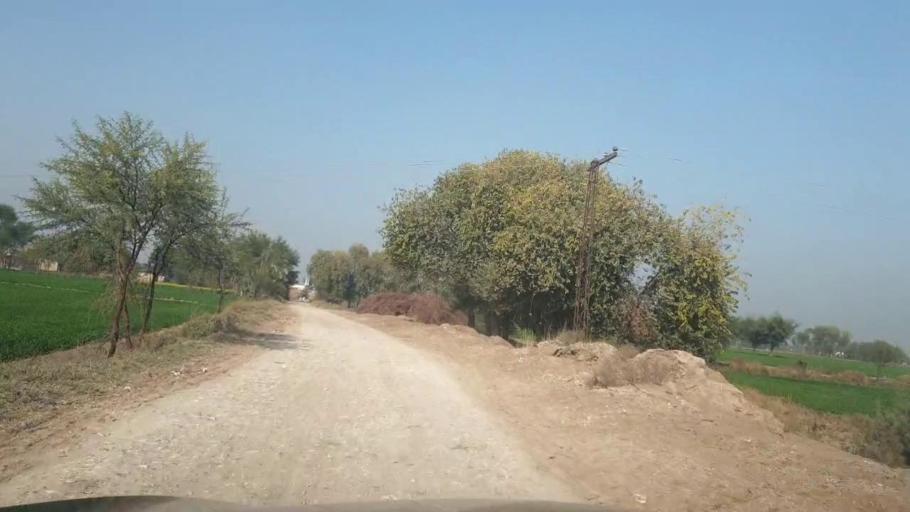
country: PK
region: Sindh
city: Ubauro
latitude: 28.0935
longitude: 69.8412
